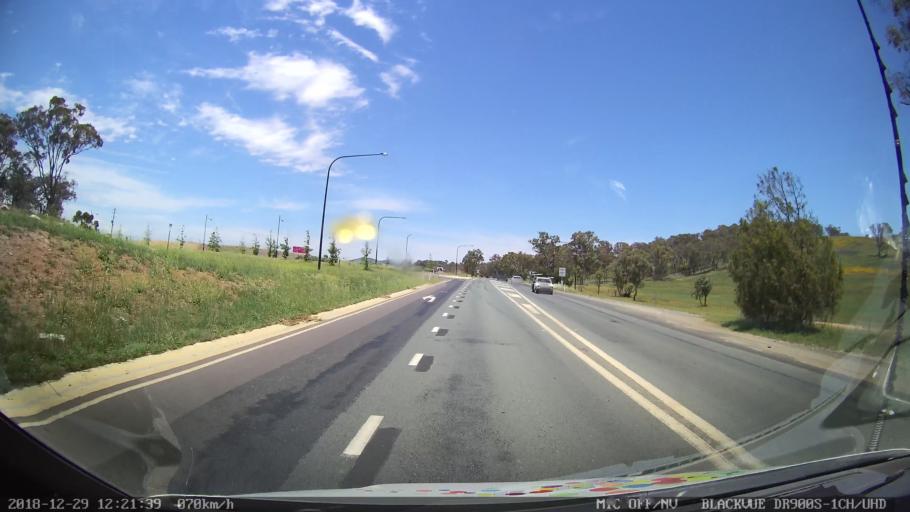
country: AU
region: New South Wales
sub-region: Queanbeyan
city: Queanbeyan
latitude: -35.4158
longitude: 149.2226
